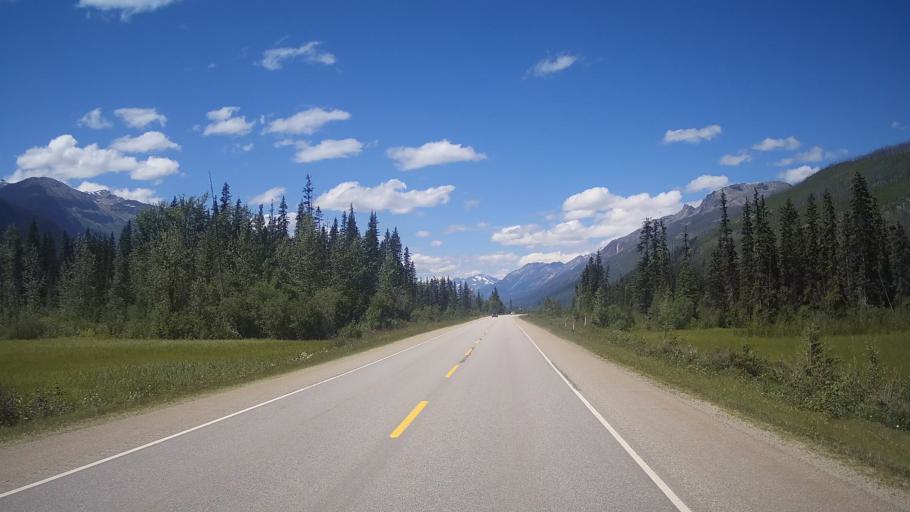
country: CA
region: Alberta
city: Jasper Park Lodge
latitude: 52.9264
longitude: -118.8195
